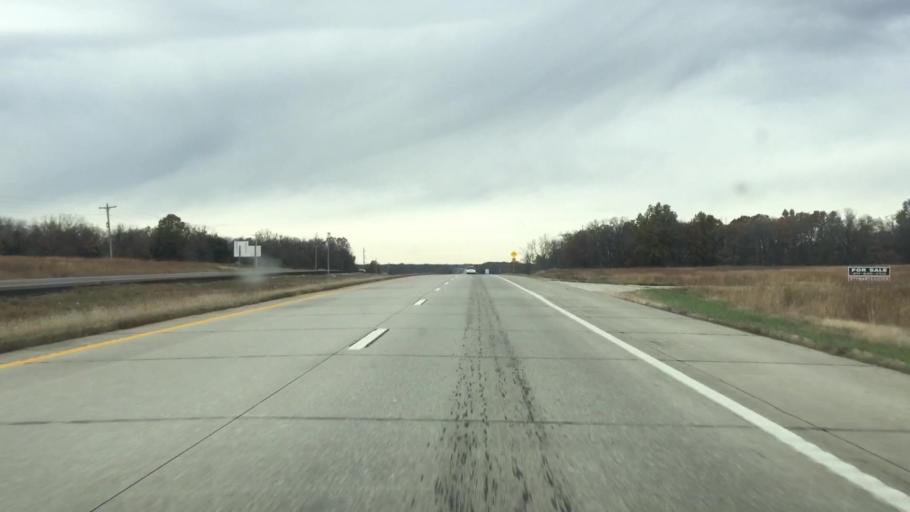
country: US
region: Missouri
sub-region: Saint Clair County
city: Osceola
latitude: 38.0456
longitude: -93.6841
